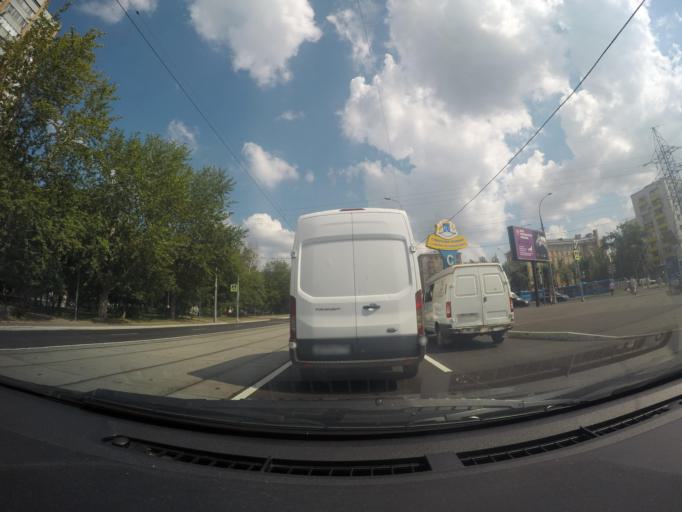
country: RU
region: Moscow
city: Rostokino
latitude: 55.8217
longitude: 37.6624
